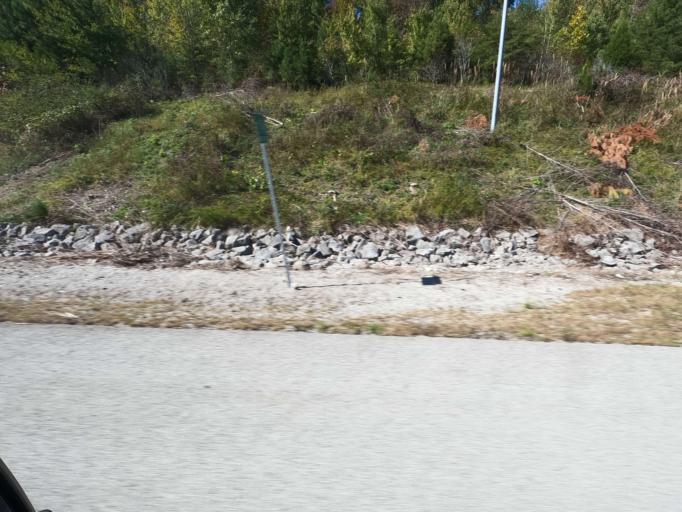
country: US
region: Tennessee
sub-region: Maury County
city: Mount Pleasant
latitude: 35.4660
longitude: -87.2665
